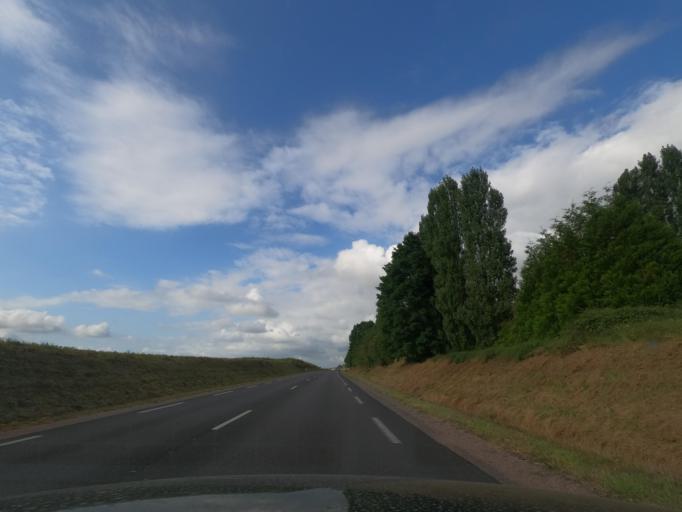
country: FR
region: Haute-Normandie
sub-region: Departement de l'Eure
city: Bernay
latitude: 49.0985
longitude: 0.5750
